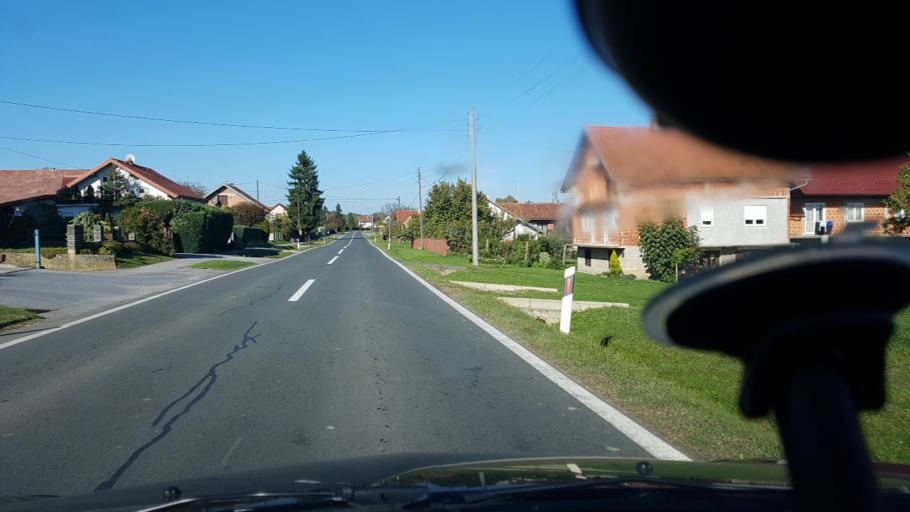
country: HR
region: Bjelovarsko-Bilogorska
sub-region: Grad Cazma
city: Cazma
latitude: 45.7754
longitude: 16.6378
